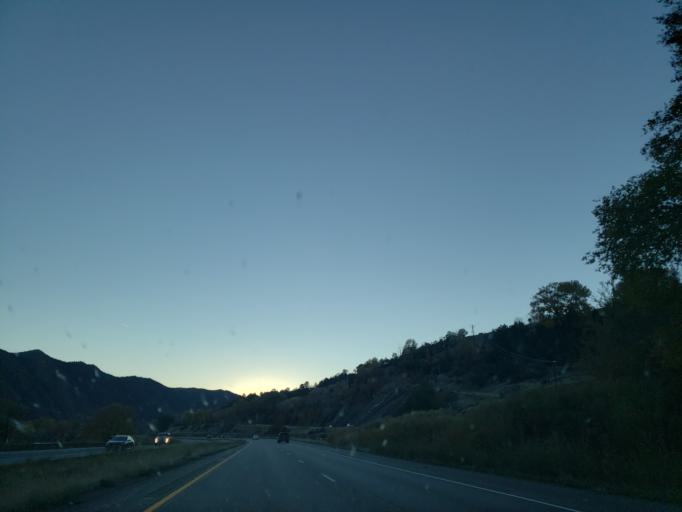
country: US
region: Colorado
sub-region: Garfield County
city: New Castle
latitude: 39.5725
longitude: -107.4782
